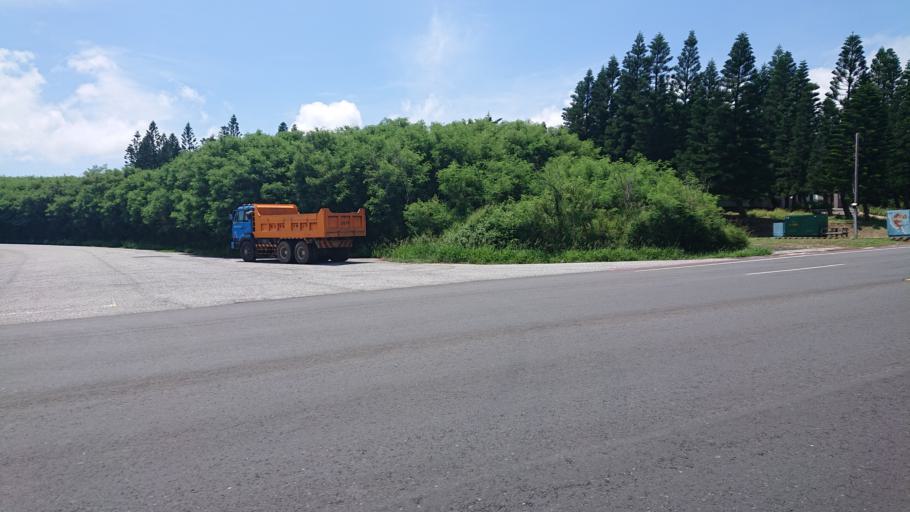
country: TW
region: Taiwan
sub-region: Penghu
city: Ma-kung
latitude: 23.6429
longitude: 119.5976
